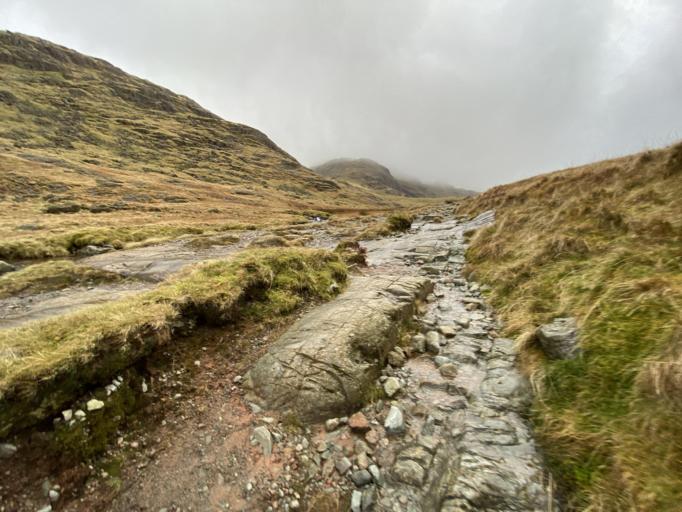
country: GB
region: England
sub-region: Cumbria
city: Keswick
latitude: 54.4806
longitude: -3.2019
